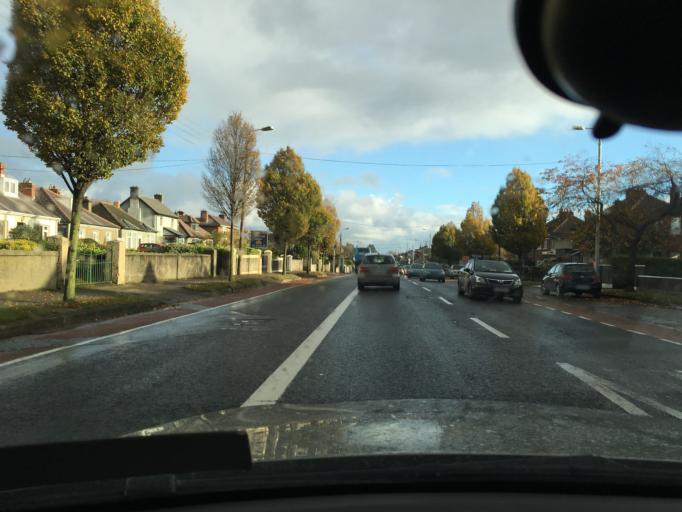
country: IE
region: Leinster
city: Cabra
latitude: 53.3660
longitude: -6.3115
